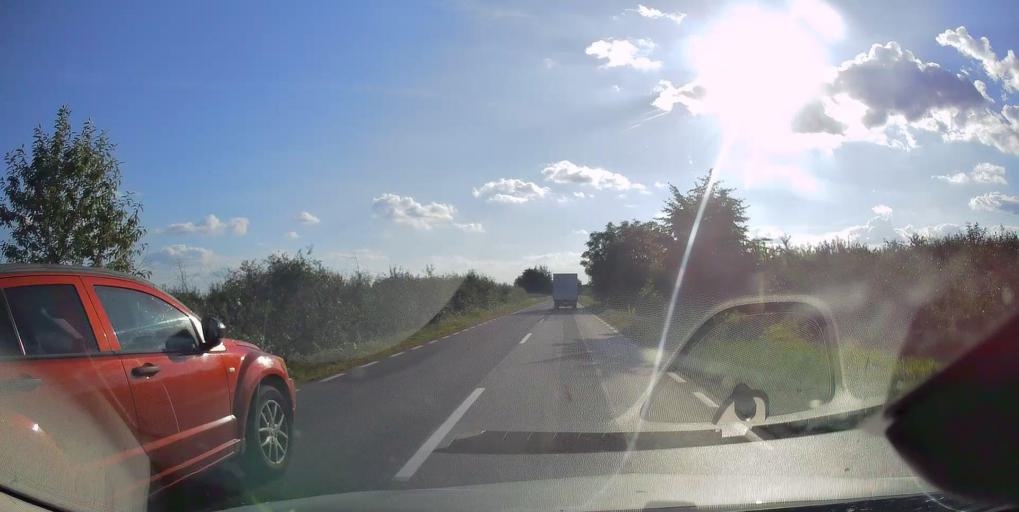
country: PL
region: Masovian Voivodeship
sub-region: Powiat grojecki
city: Bledow
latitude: 51.8084
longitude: 20.6673
